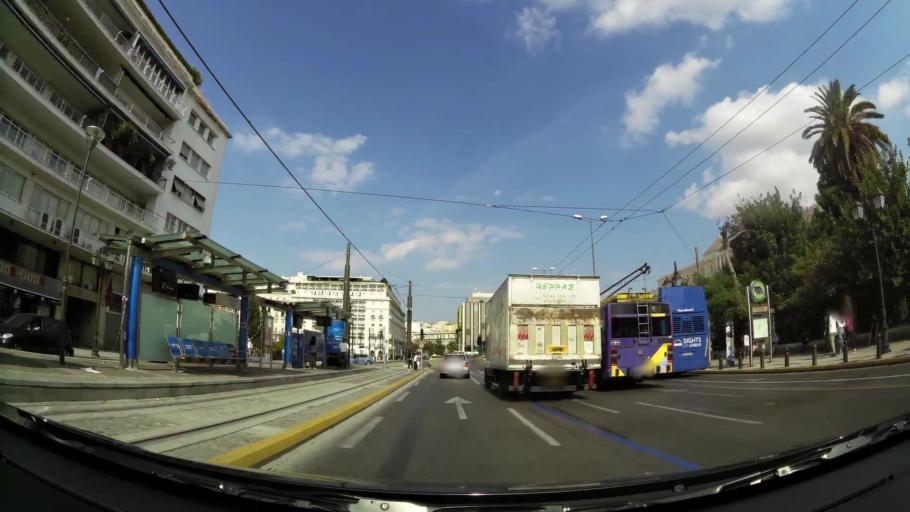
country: GR
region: Attica
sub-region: Nomarchia Athinas
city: Athens
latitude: 37.9745
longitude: 23.7355
